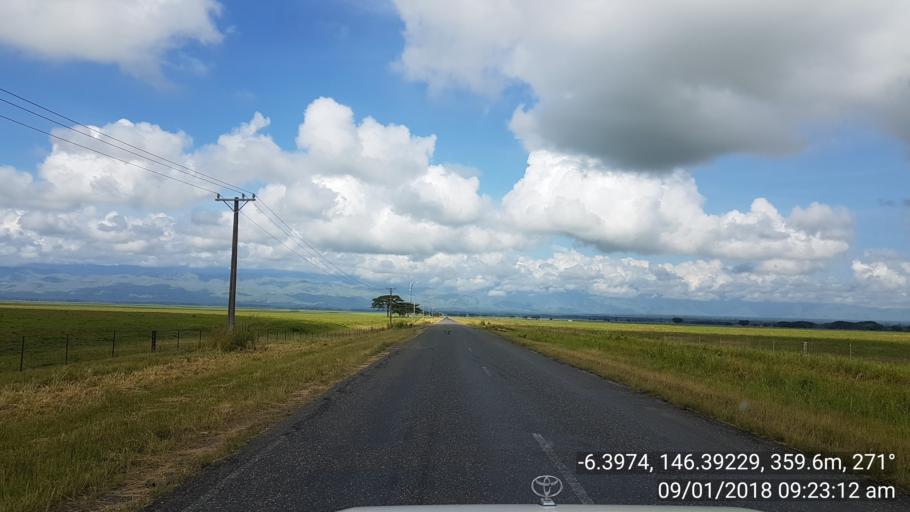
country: PG
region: Eastern Highlands
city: Kainantu
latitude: -6.3973
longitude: 146.3916
